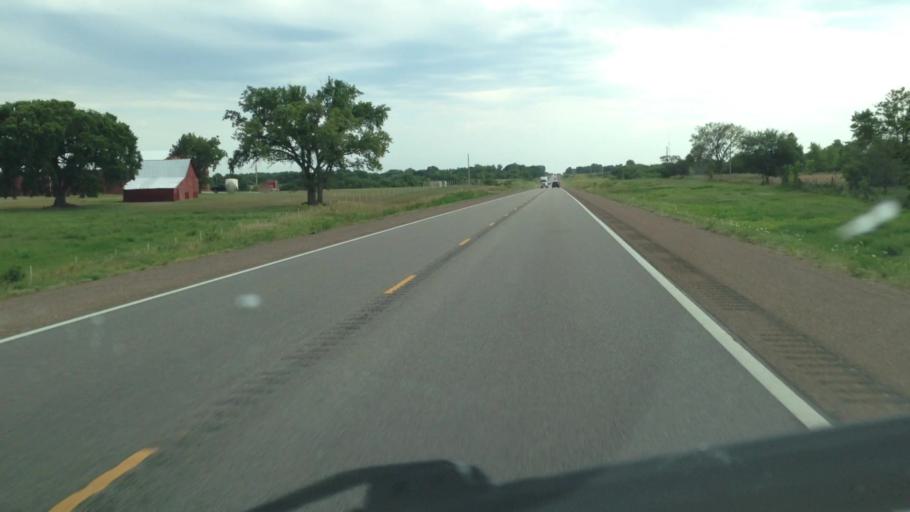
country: US
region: Kansas
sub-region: Woodson County
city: Yates Center
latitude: 38.0024
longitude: -95.7389
